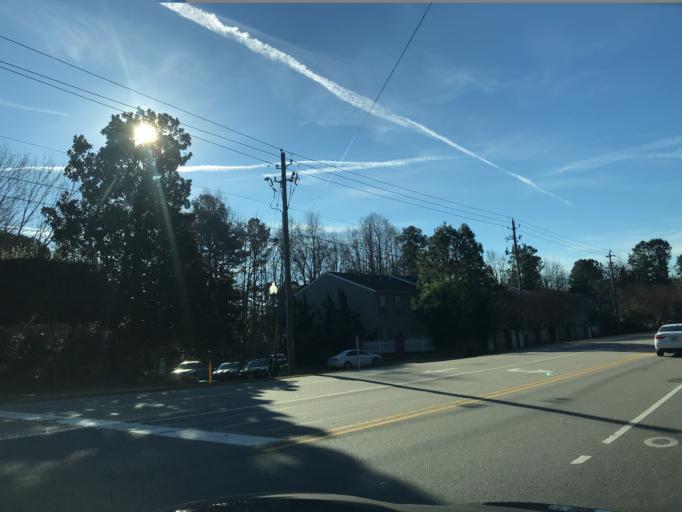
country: US
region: North Carolina
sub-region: Wake County
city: Wake Forest
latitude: 35.8956
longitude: -78.5996
